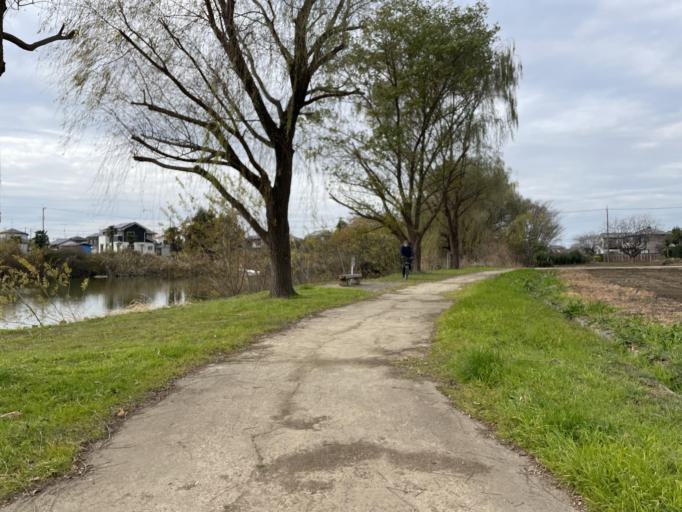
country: JP
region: Saitama
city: Shiraoka
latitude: 36.0225
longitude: 139.6428
